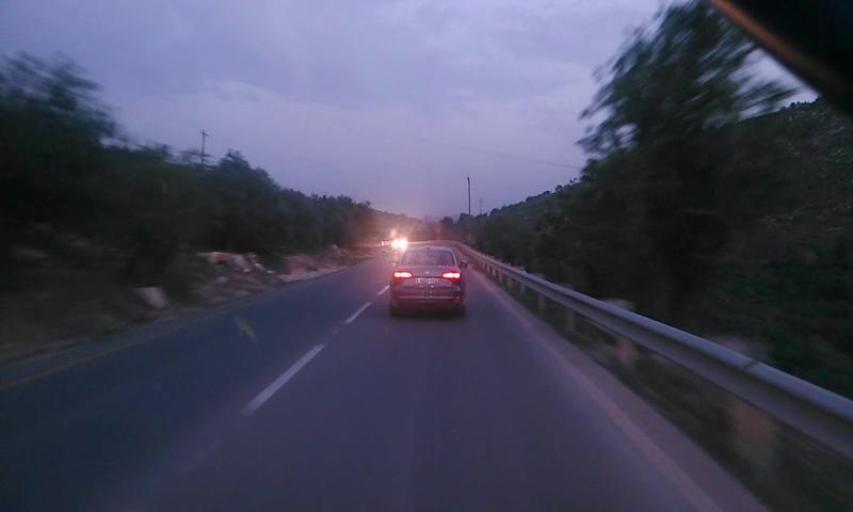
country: PS
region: West Bank
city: Ramin
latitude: 32.2812
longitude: 35.1439
